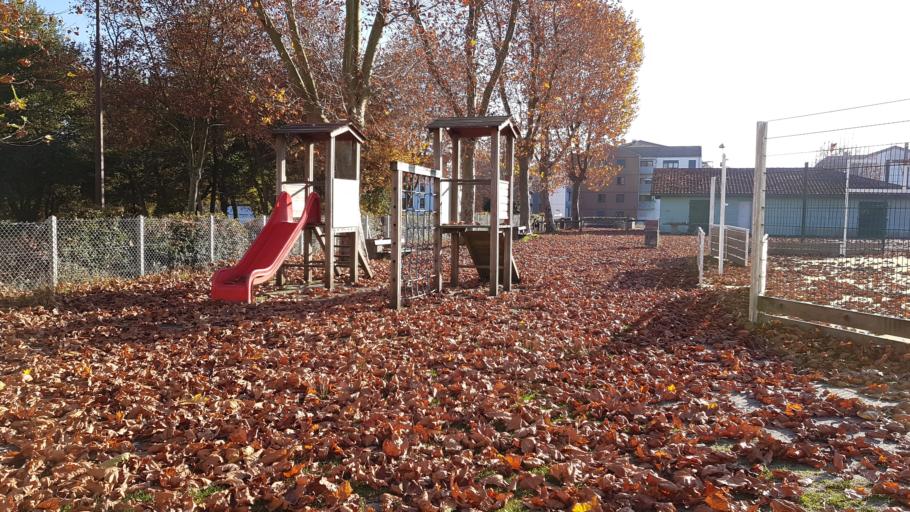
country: FR
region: Aquitaine
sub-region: Departement des Landes
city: Saint-Paul-les-Dax
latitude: 43.7252
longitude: -1.0786
